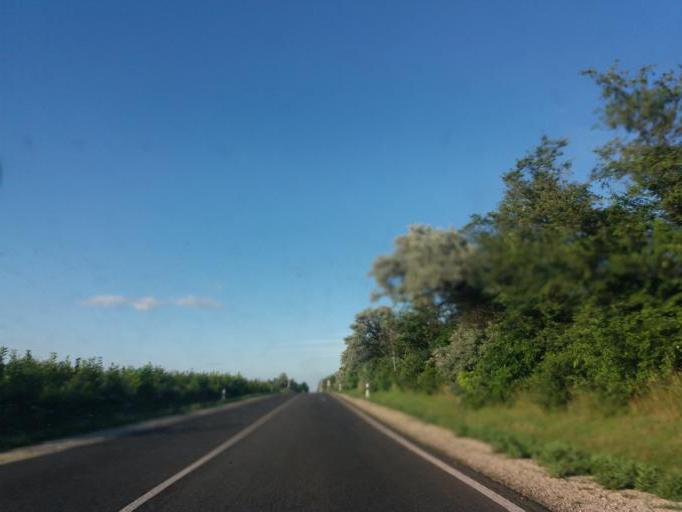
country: HU
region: Fejer
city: Baracska
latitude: 47.2732
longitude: 18.7381
